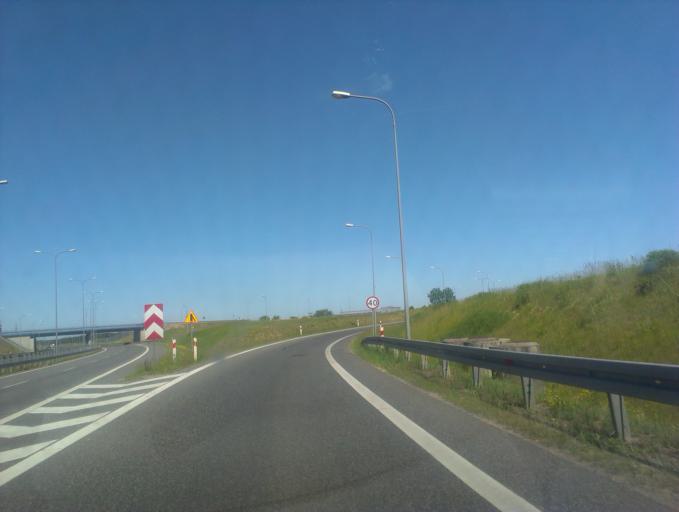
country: PL
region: Pomeranian Voivodeship
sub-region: Powiat chojnicki
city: Chojnice
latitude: 53.6880
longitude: 17.6164
